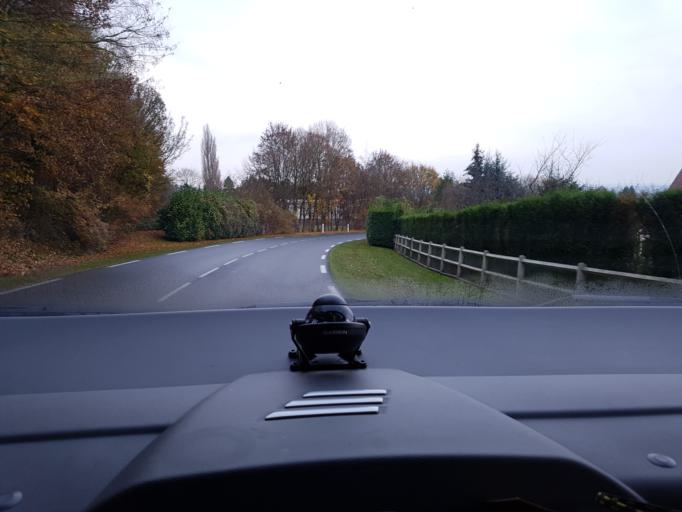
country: FR
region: Haute-Normandie
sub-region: Departement de la Seine-Maritime
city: Duclair
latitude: 49.4878
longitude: 0.8877
